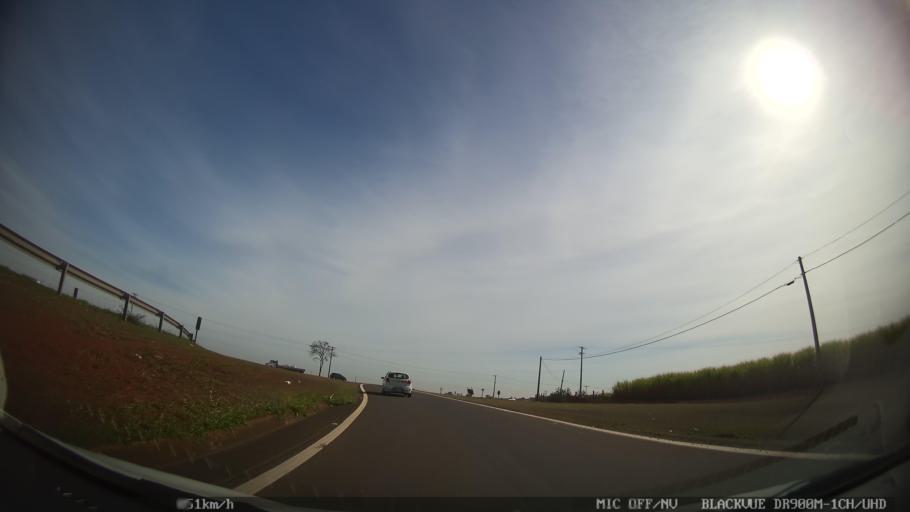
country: BR
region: Sao Paulo
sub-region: Piracicaba
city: Piracicaba
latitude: -22.7810
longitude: -47.6519
